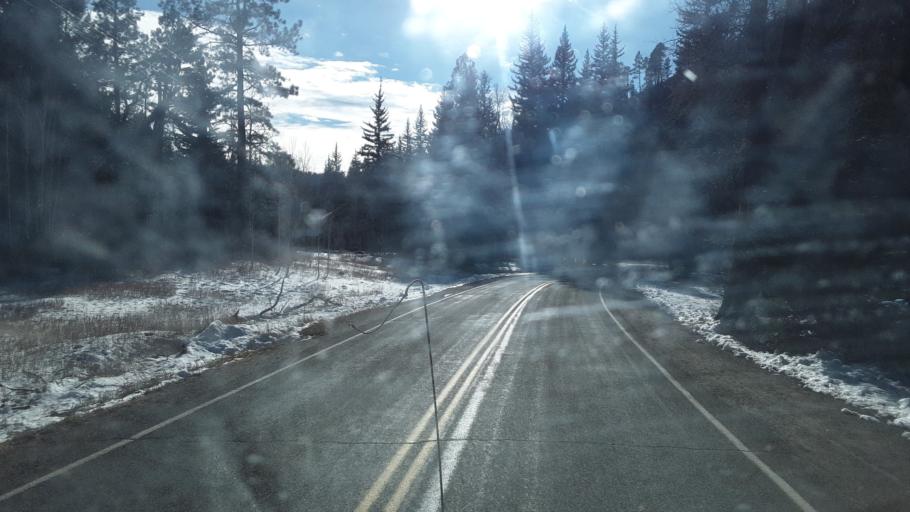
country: US
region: Colorado
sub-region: La Plata County
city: Bayfield
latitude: 37.3715
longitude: -107.6640
